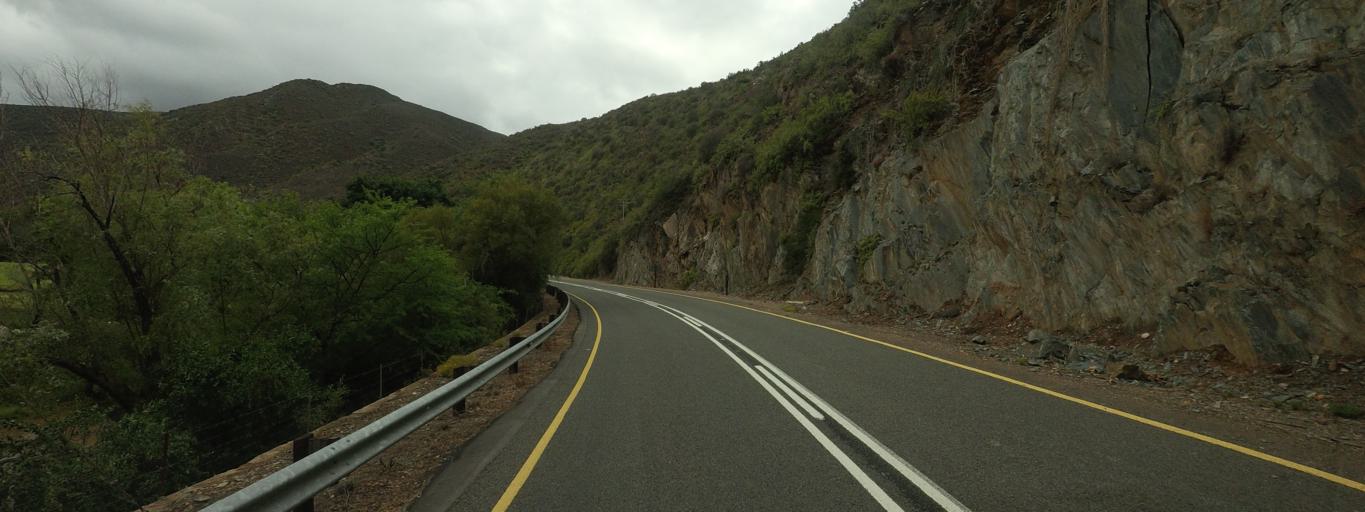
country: ZA
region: Western Cape
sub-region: Eden District Municipality
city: Oudtshoorn
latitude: -33.4613
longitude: 22.2538
